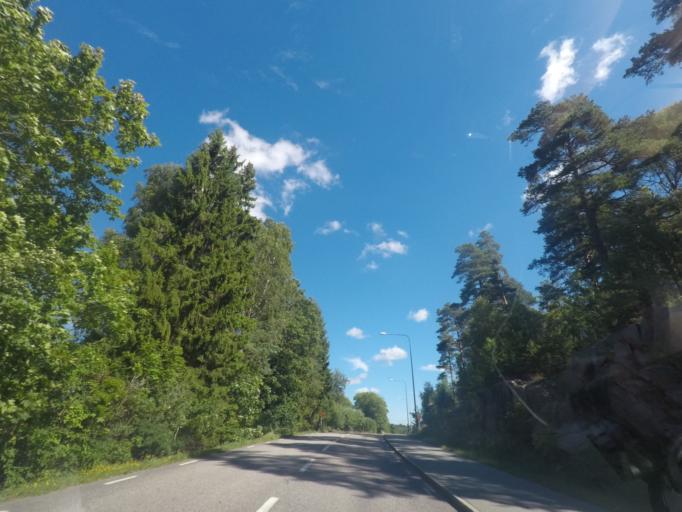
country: SE
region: Uppsala
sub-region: Knivsta Kommun
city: Knivsta
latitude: 59.8774
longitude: 17.9652
